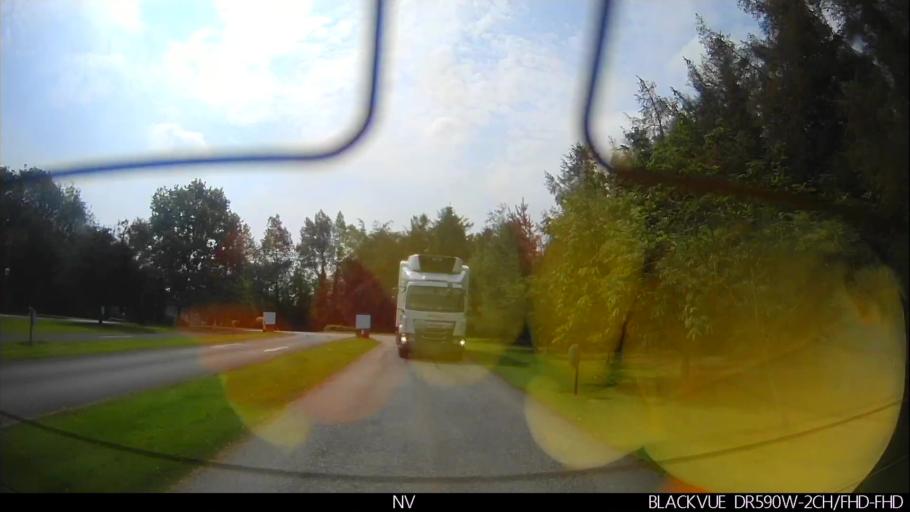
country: GB
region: England
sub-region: North Yorkshire
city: Great Habton
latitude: 54.2061
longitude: -0.8095
